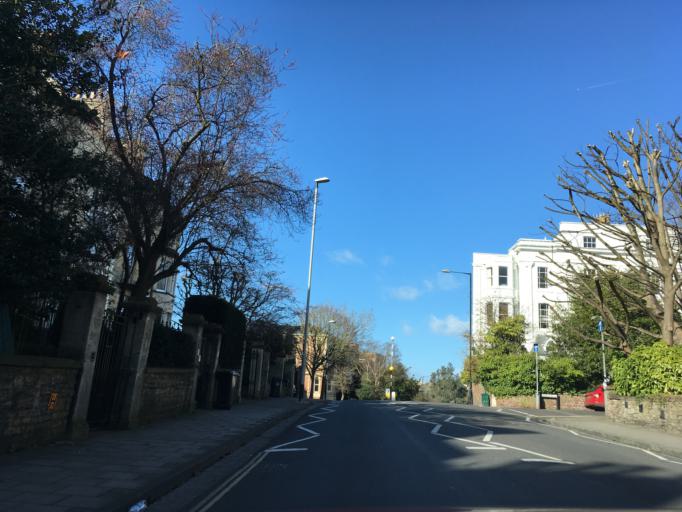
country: GB
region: England
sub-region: Bristol
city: Bristol
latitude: 51.4594
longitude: -2.6153
